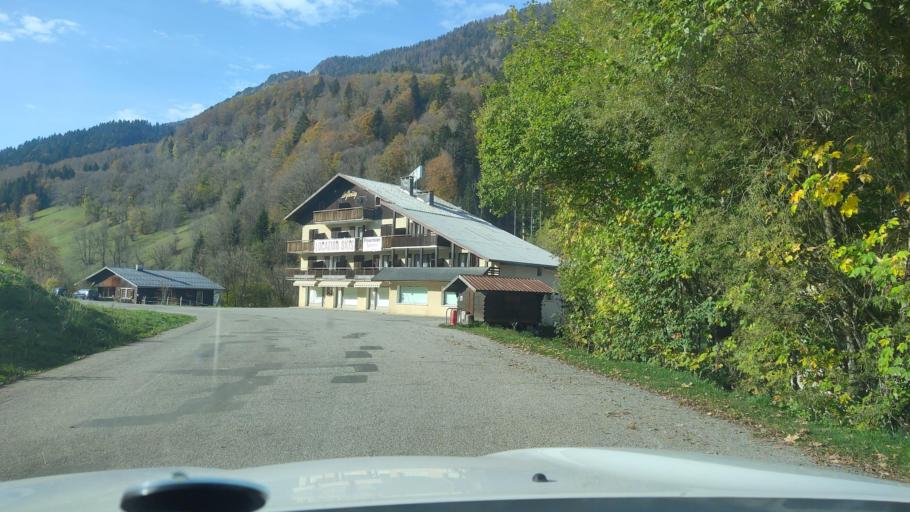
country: FR
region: Rhone-Alpes
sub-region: Departement de la Savoie
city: Cruet
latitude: 45.6081
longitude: 6.1007
